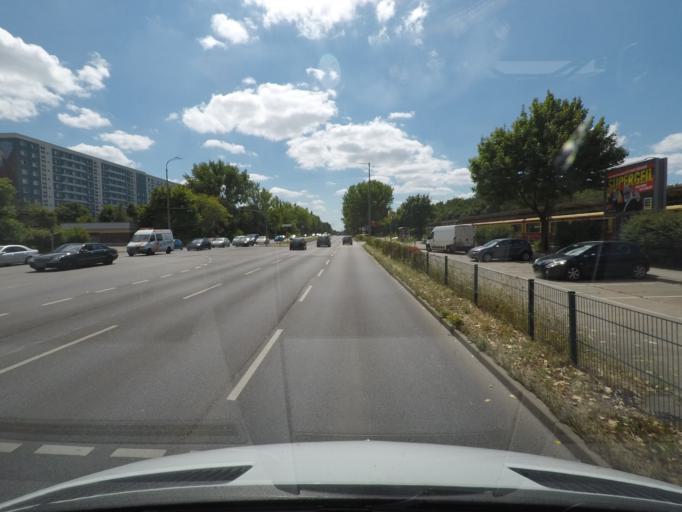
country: DE
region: Berlin
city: Falkenberg
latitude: 52.5510
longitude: 13.5483
